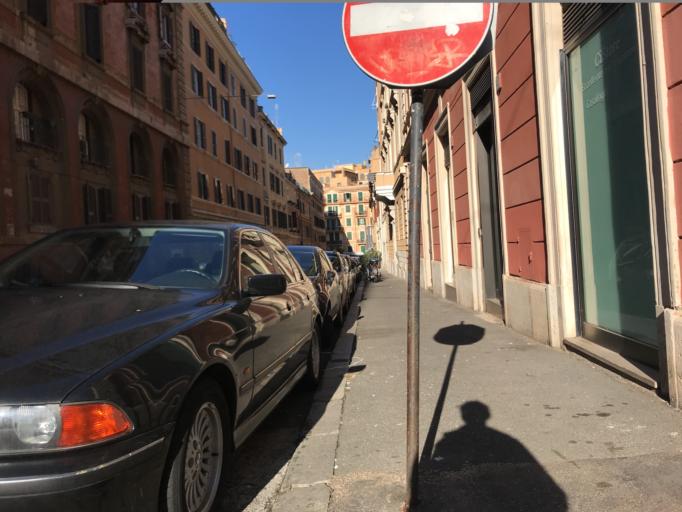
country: IT
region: Latium
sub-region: Citta metropolitana di Roma Capitale
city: Rome
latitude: 41.9122
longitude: 12.5032
